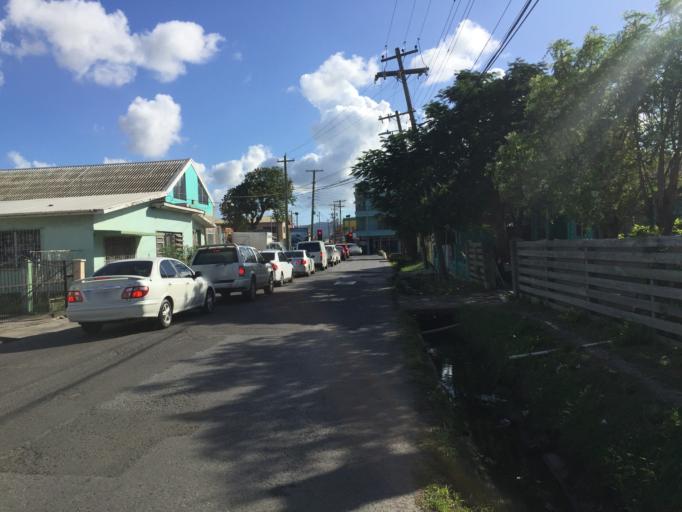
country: AG
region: Saint John
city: Saint John's
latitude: 17.1267
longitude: -61.8448
